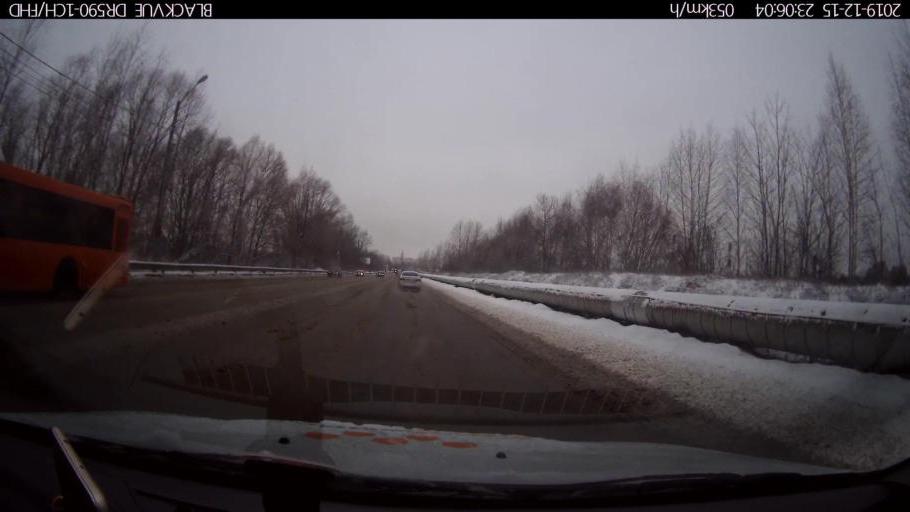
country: RU
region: Nizjnij Novgorod
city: Nizhniy Novgorod
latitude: 56.3424
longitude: 43.9024
